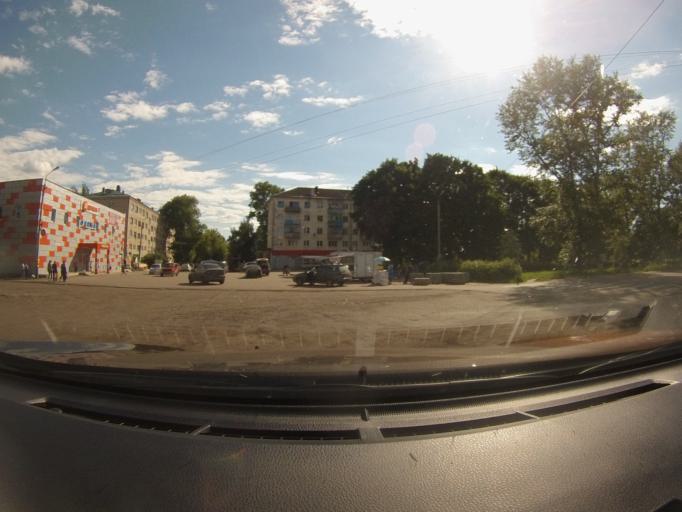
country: RU
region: Orjol
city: Mtsensk
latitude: 53.2749
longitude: 36.5756
